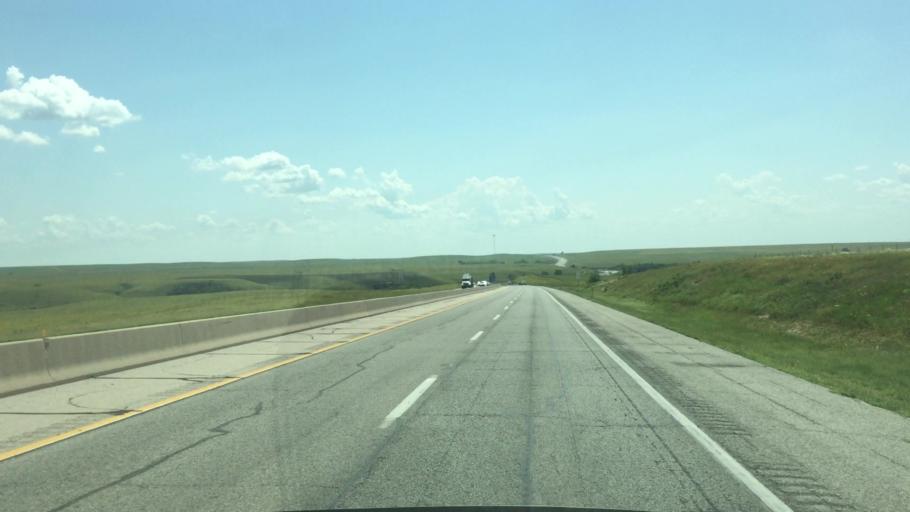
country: US
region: Kansas
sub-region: Chase County
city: Cottonwood Falls
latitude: 38.1851
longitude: -96.4576
